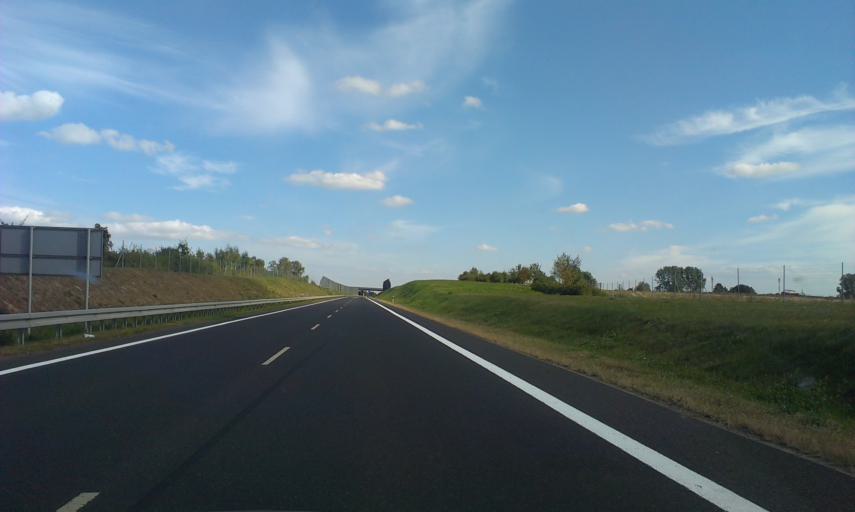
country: PL
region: Greater Poland Voivodeship
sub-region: Powiat pilski
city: Wyrzysk
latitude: 53.1629
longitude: 17.2557
